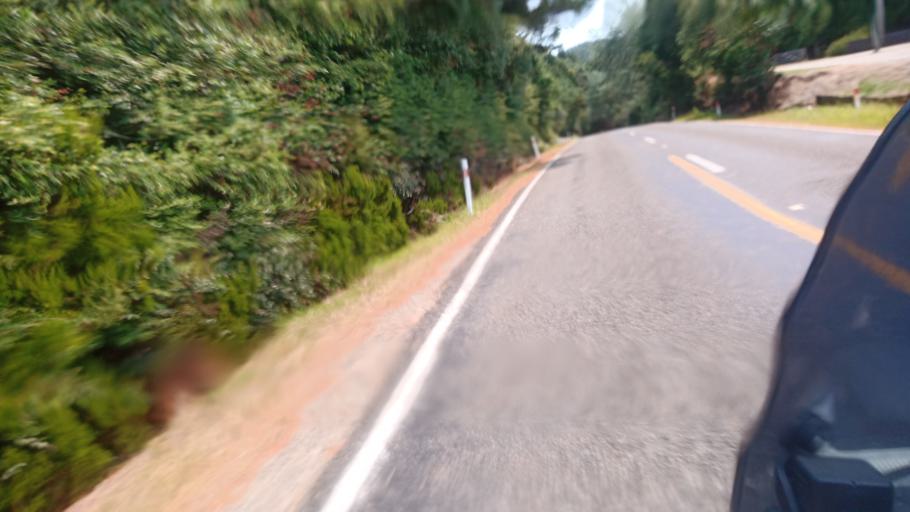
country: NZ
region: Bay of Plenty
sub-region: Opotiki District
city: Opotiki
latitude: -37.5737
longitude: 178.1426
